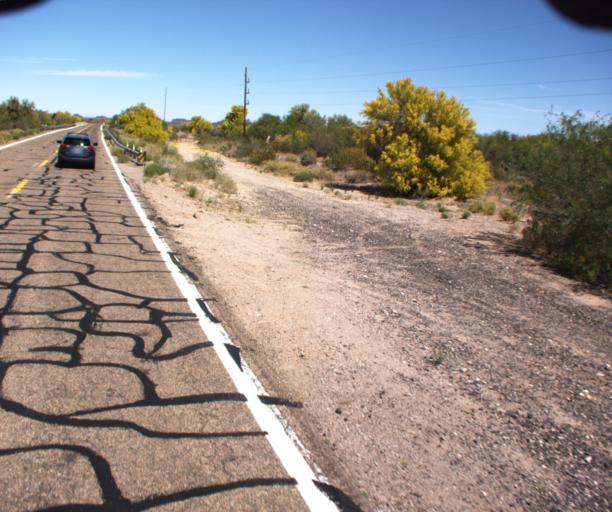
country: US
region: Arizona
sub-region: Pima County
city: Ajo
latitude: 32.4973
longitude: -112.8816
